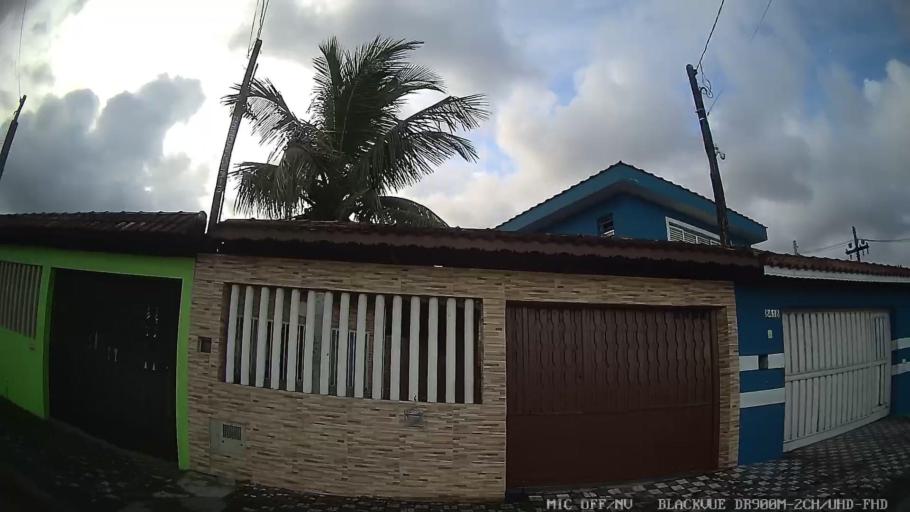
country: BR
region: Sao Paulo
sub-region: Mongagua
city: Mongagua
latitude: -24.1172
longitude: -46.6738
